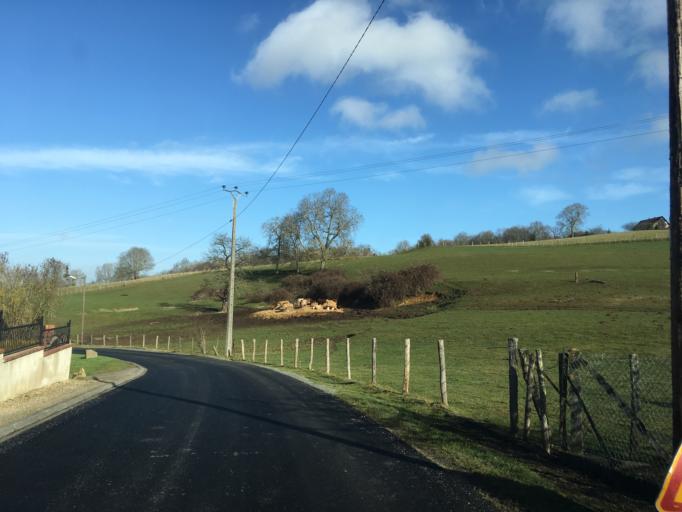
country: FR
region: Haute-Normandie
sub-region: Departement de l'Eure
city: Saint-Just
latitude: 49.1249
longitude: 1.4076
